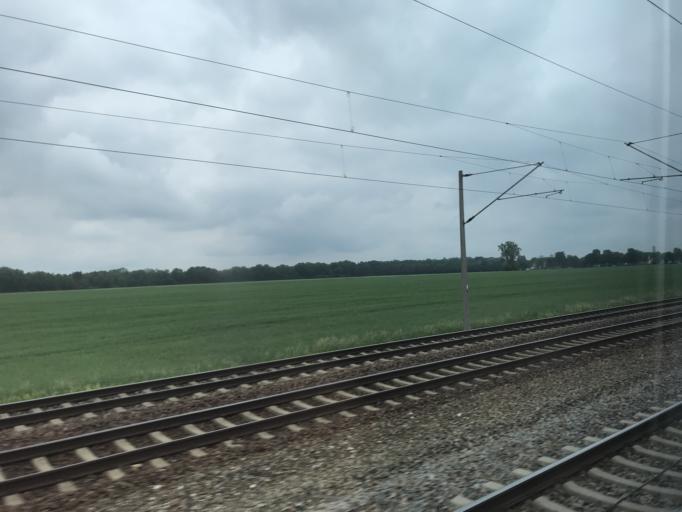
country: DE
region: Bavaria
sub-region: Swabia
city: Kissing
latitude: 48.3312
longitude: 10.9541
